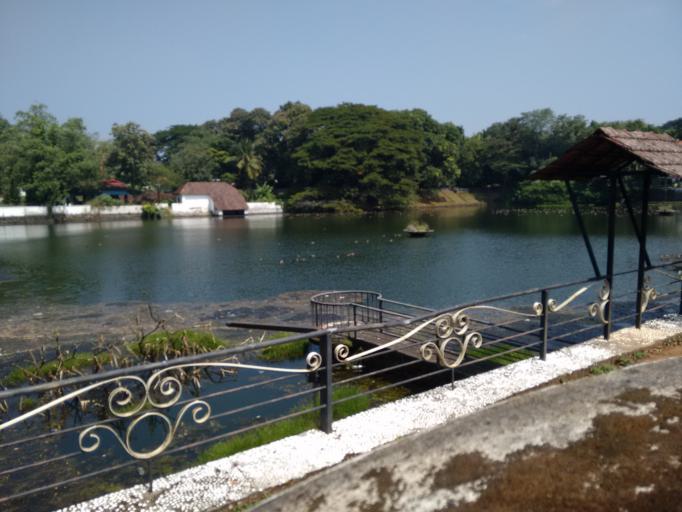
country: IN
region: Kerala
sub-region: Thrissur District
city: Trichur
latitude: 10.5295
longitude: 76.2151
